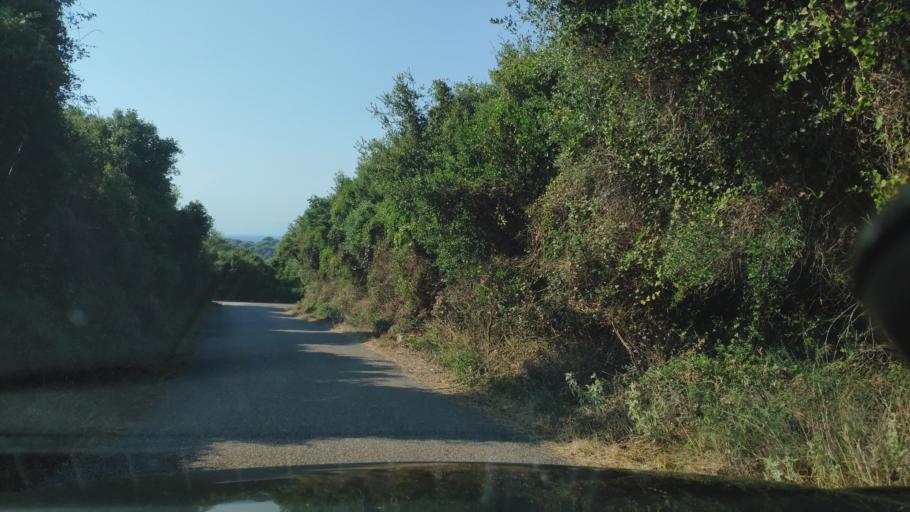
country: GR
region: West Greece
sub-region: Nomos Aitolias kai Akarnanias
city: Amfilochia
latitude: 38.9031
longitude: 21.1125
